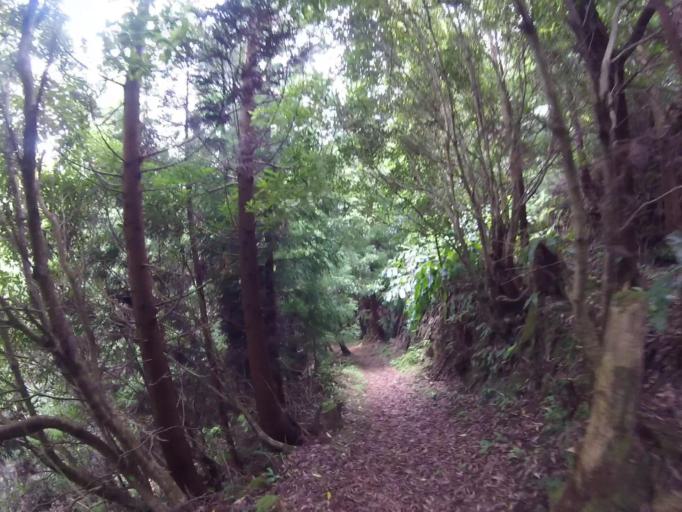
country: PT
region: Azores
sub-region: Vila Franca do Campo
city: Vila Franca do Campo
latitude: 37.7463
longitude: -25.5096
